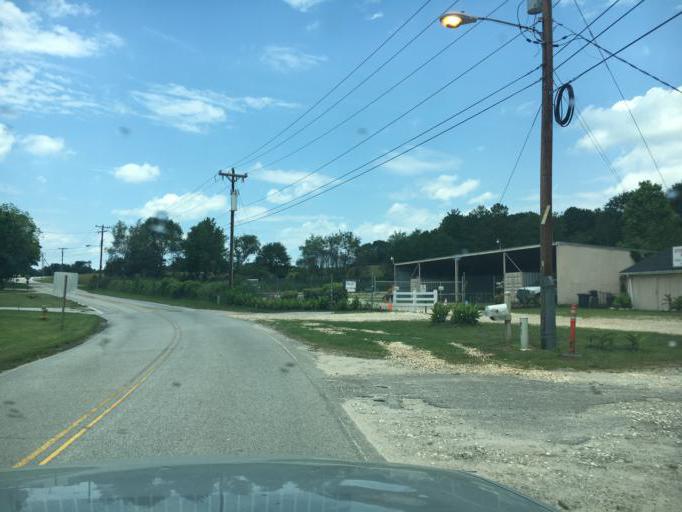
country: US
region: South Carolina
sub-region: Greenville County
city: Five Forks
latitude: 34.8720
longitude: -82.2425
